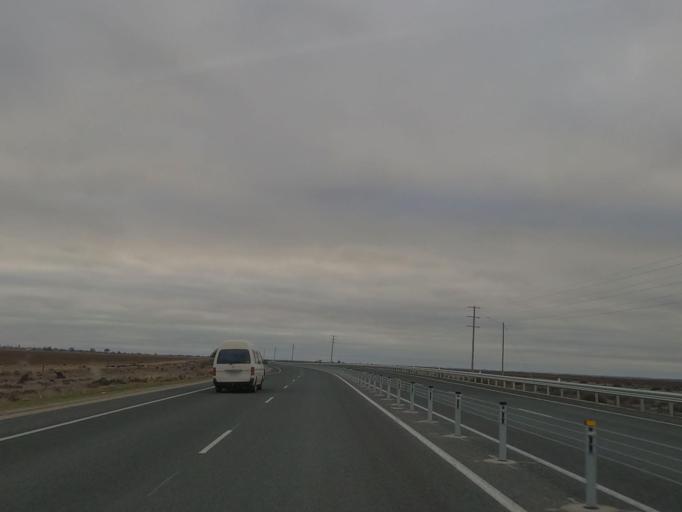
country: AU
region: Victoria
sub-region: Swan Hill
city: Swan Hill
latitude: -35.5103
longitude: 143.7240
